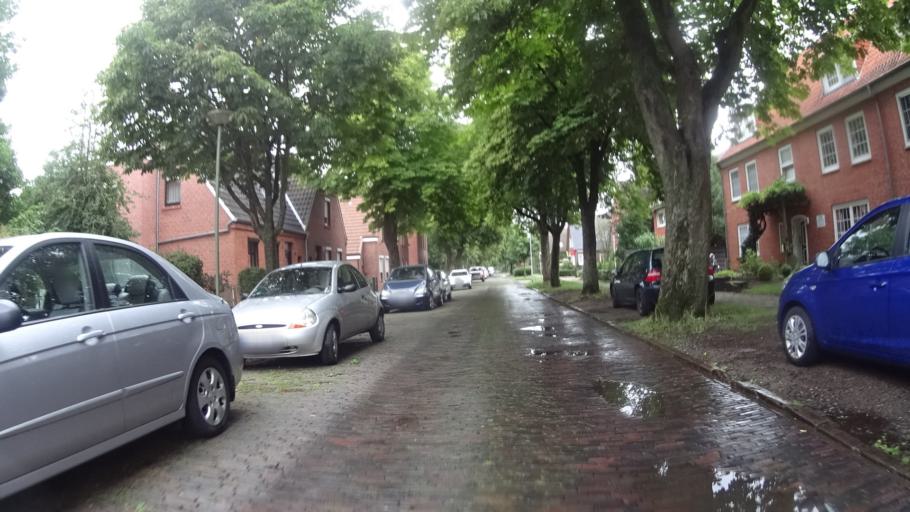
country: DE
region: Lower Saxony
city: Leer
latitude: 53.2314
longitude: 7.4451
